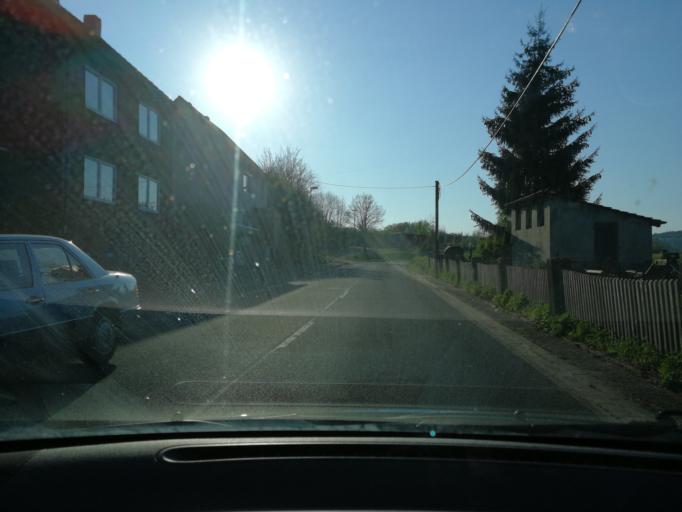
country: DE
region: Lower Saxony
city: Uslar
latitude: 51.6140
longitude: 9.6656
